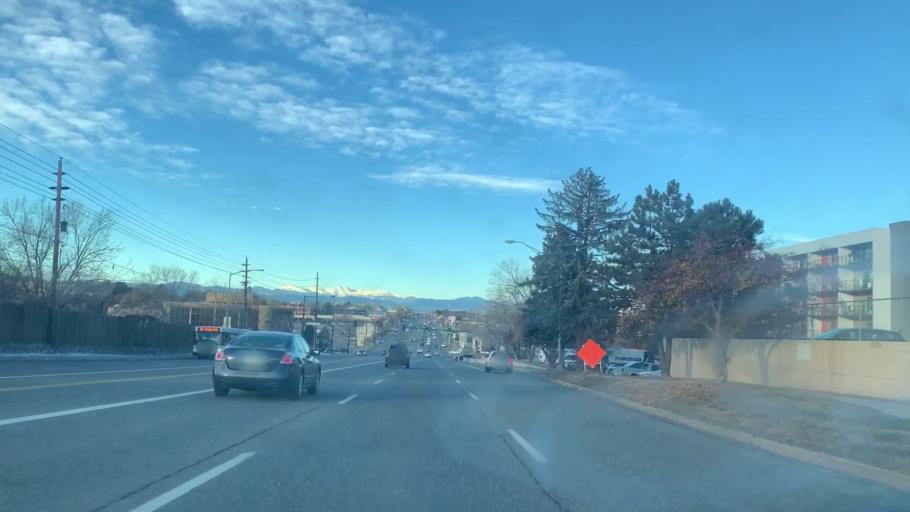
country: US
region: Colorado
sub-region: Arapahoe County
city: Glendale
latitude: 39.6532
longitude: -104.8970
